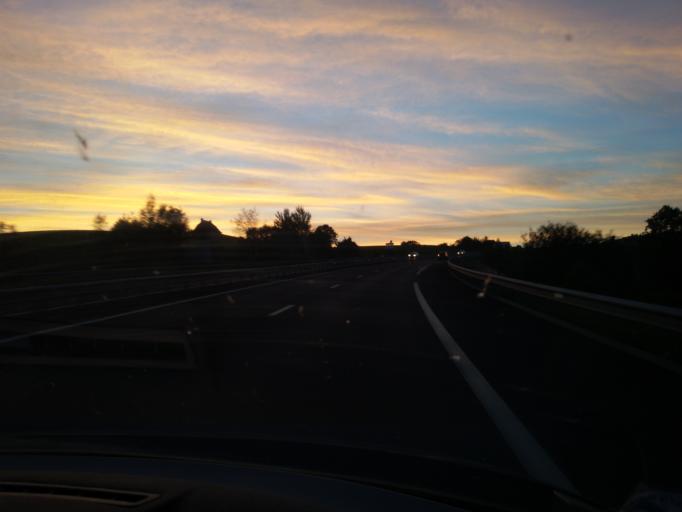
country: FR
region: Auvergne
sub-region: Departement du Cantal
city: Saint-Flour
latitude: 45.0377
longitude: 3.1224
